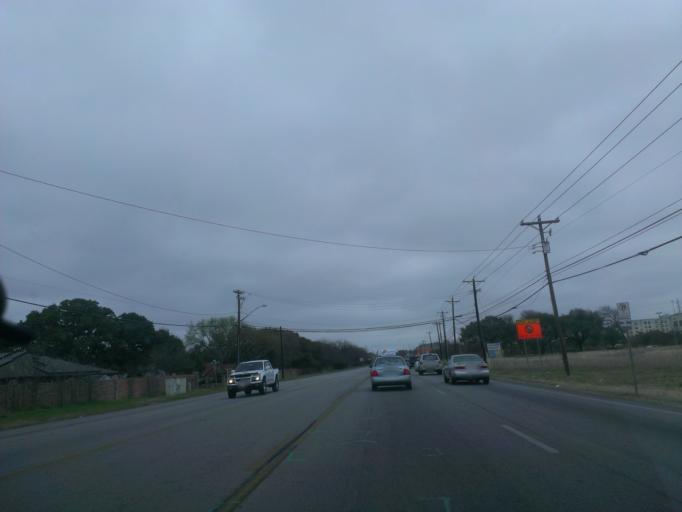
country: US
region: Texas
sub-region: Travis County
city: Wells Branch
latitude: 30.4027
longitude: -97.6790
